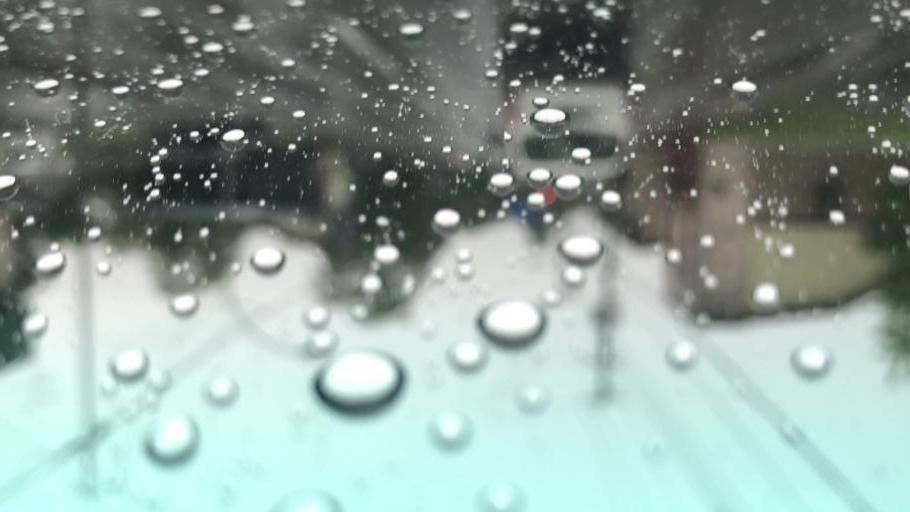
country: JP
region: Hokkaido
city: Nayoro
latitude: 44.2910
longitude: 142.4181
